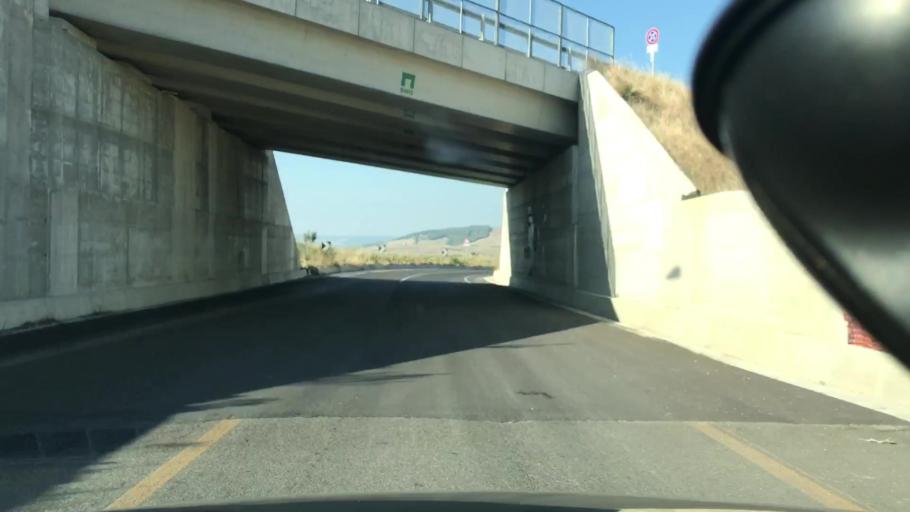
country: IT
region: Basilicate
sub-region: Provincia di Matera
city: La Martella
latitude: 40.6573
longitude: 16.5606
